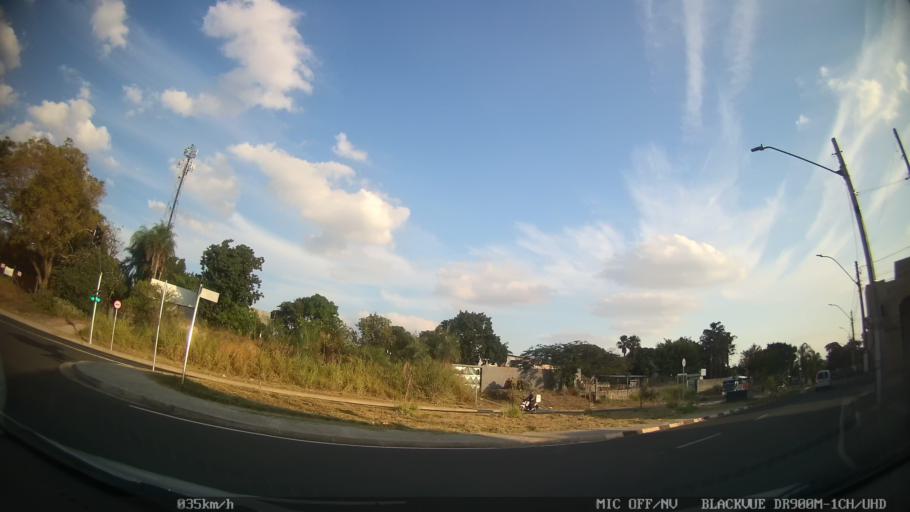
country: BR
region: Sao Paulo
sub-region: Hortolandia
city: Hortolandia
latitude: -22.8847
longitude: -47.1604
